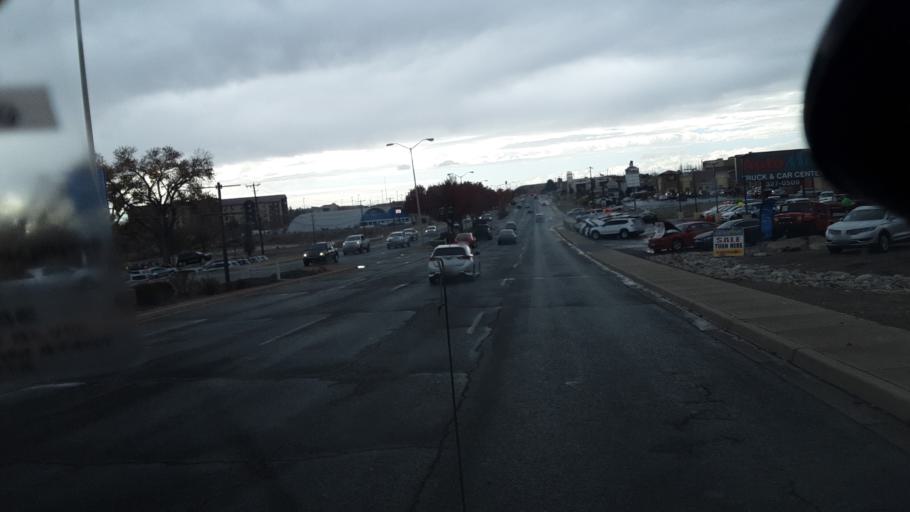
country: US
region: New Mexico
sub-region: San Juan County
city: Flora Vista
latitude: 36.7703
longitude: -108.1418
